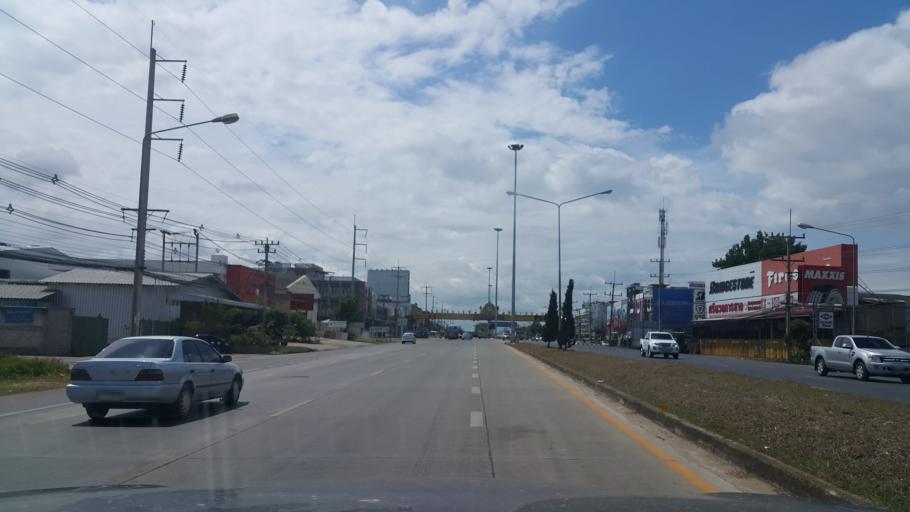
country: TH
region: Phayao
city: Phayao
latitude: 19.1728
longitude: 99.9054
